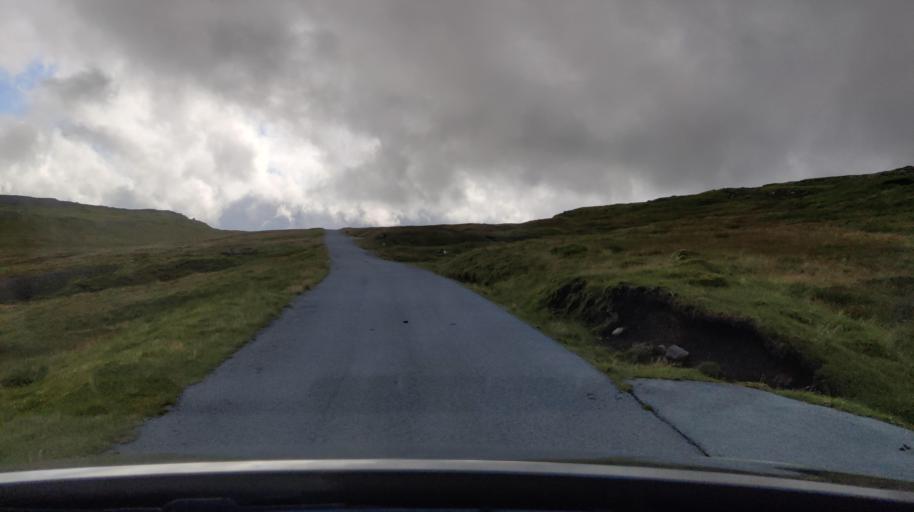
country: FO
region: Streymoy
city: Vestmanna
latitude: 62.1720
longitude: -7.1586
